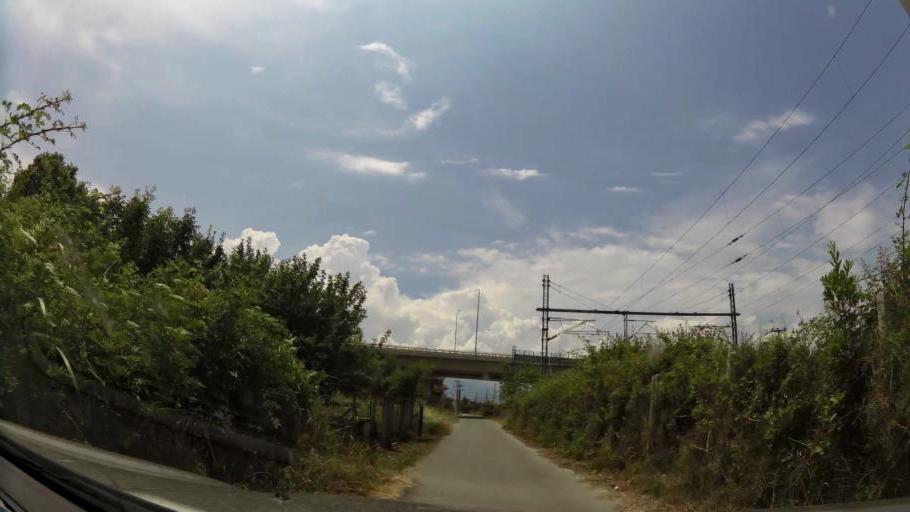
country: GR
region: Central Macedonia
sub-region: Nomos Pierias
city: Peristasi
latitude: 40.2745
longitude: 22.5359
